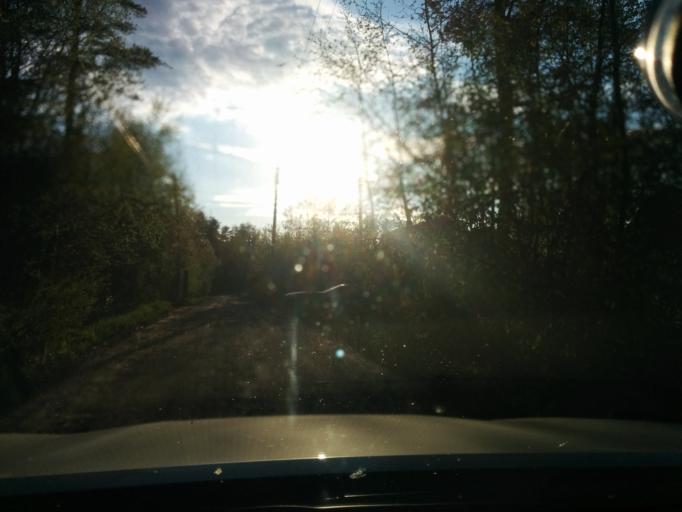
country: RU
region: Leningrad
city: Verkhniye Osel'ki
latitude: 60.2596
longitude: 30.4165
